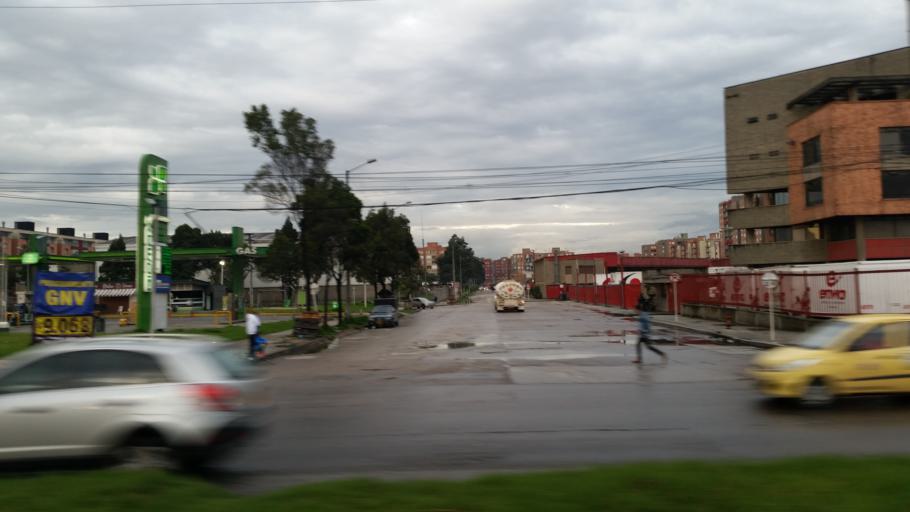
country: CO
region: Bogota D.C.
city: Bogota
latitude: 4.6617
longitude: -74.1379
